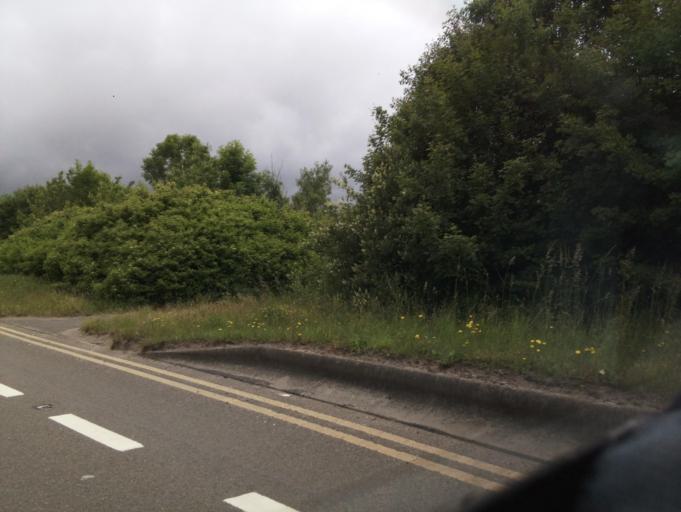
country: GB
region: England
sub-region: Leicestershire
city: Ashby de la Zouch
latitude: 52.7651
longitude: -1.4954
